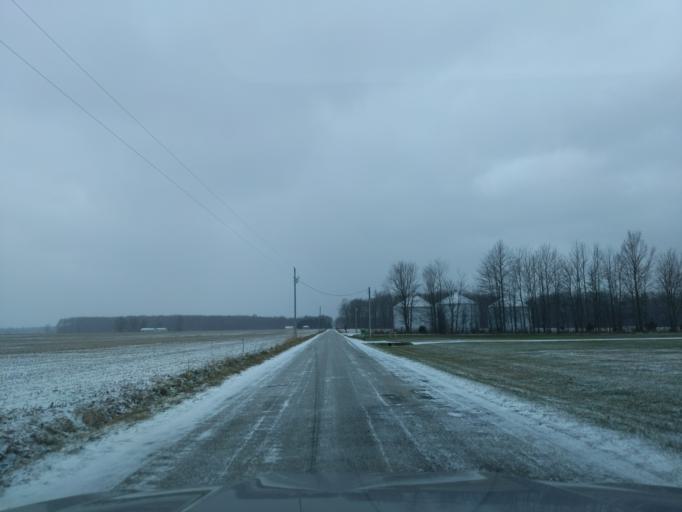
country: US
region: Indiana
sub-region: Decatur County
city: Greensburg
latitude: 39.2340
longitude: -85.4729
